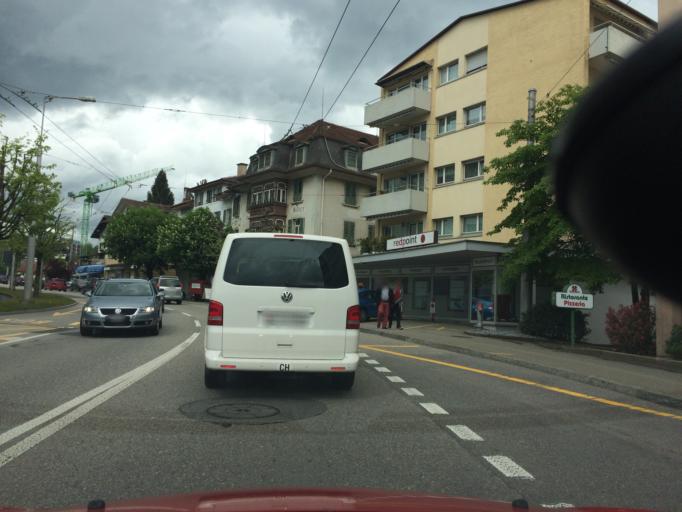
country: CH
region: Lucerne
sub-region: Hochdorf District
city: Emmen
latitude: 47.0777
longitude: 8.2757
